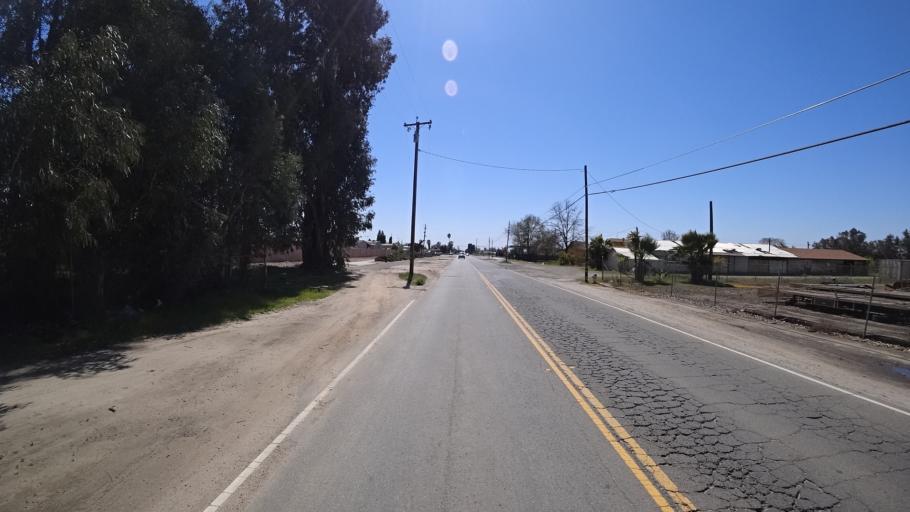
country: US
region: California
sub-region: Fresno County
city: West Park
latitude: 36.7594
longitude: -119.8444
